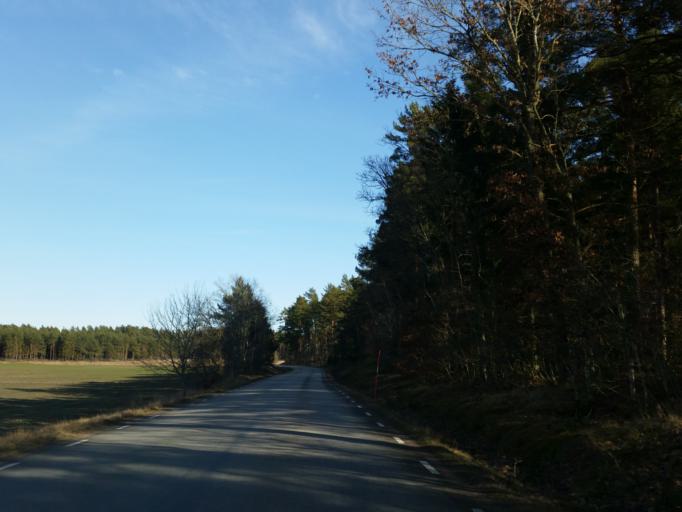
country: SE
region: Kalmar
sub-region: Kalmar Kommun
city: Lindsdal
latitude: 56.7868
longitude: 16.3756
